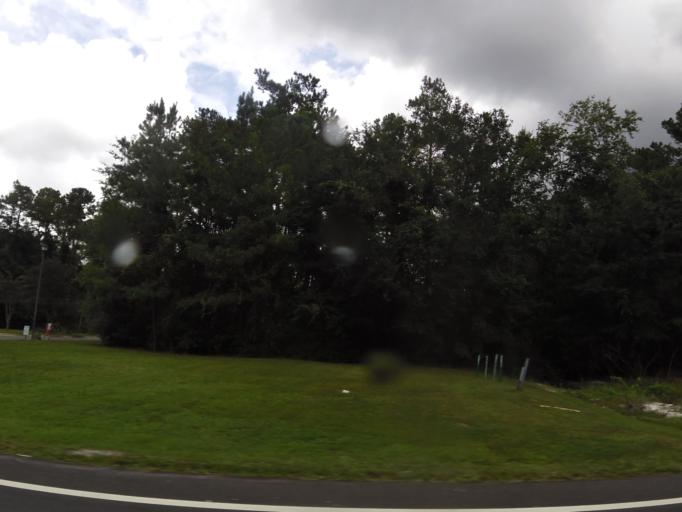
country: US
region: Florida
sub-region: Clay County
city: Middleburg
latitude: 30.0489
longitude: -81.8538
